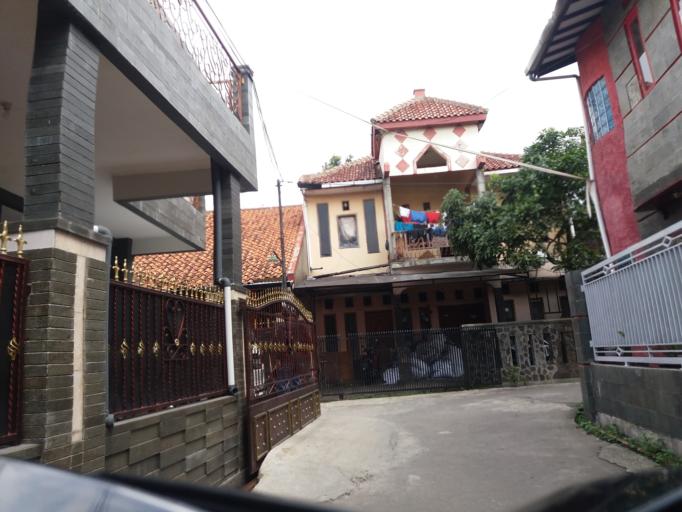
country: ID
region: West Java
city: Bandung
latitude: -6.9255
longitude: 107.6592
